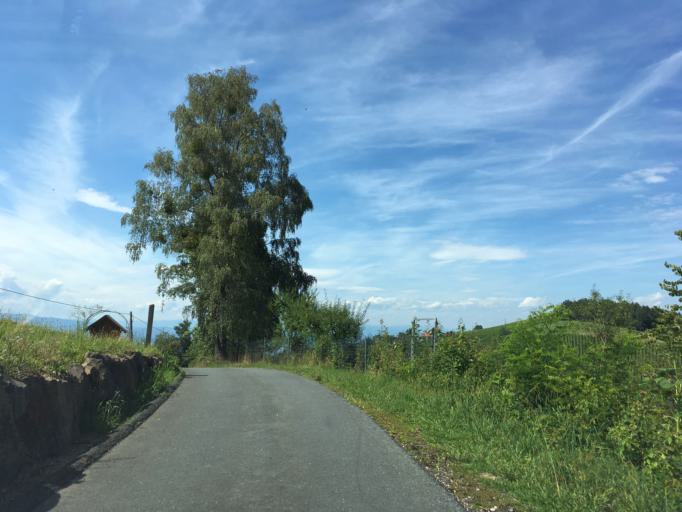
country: AT
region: Styria
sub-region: Politischer Bezirk Leibnitz
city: Kitzeck im Sausal
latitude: 46.7910
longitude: 15.4257
